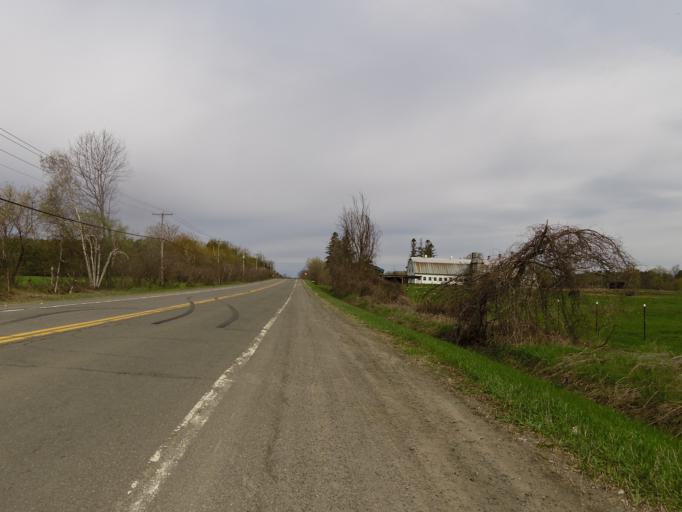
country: CA
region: Quebec
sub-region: Laurentides
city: Oka
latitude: 45.4694
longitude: -74.1183
